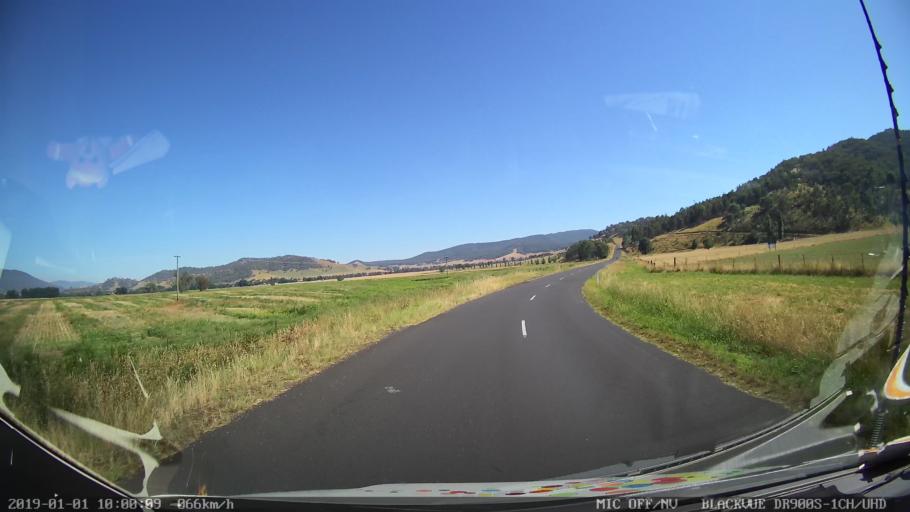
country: AU
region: New South Wales
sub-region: Snowy River
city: Jindabyne
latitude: -36.2051
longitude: 148.1021
